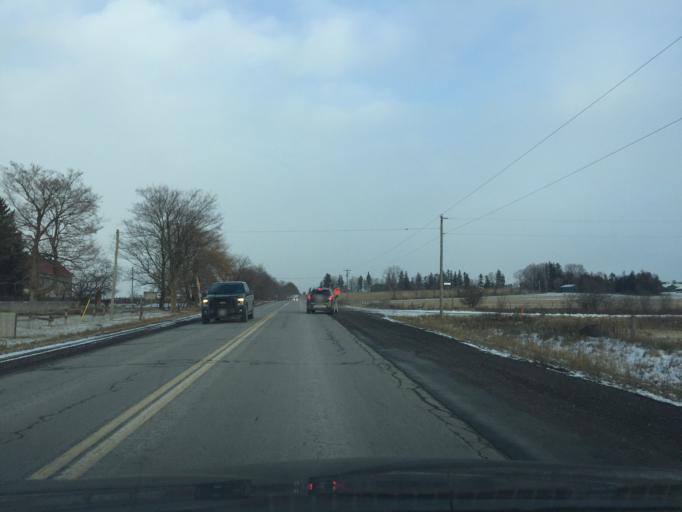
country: CA
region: Ontario
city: Uxbridge
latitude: 44.0746
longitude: -78.9979
